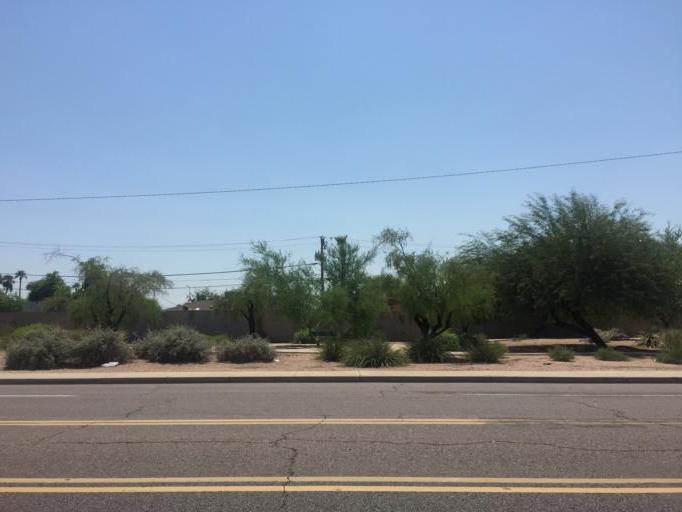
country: US
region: Arizona
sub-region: Maricopa County
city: Phoenix
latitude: 33.5057
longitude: -112.0407
